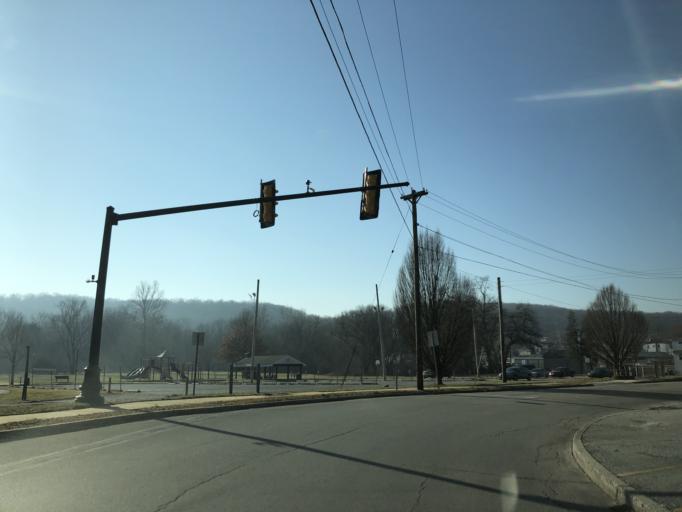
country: US
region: Pennsylvania
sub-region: Chester County
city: Downingtown
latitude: 40.0024
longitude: -75.7077
